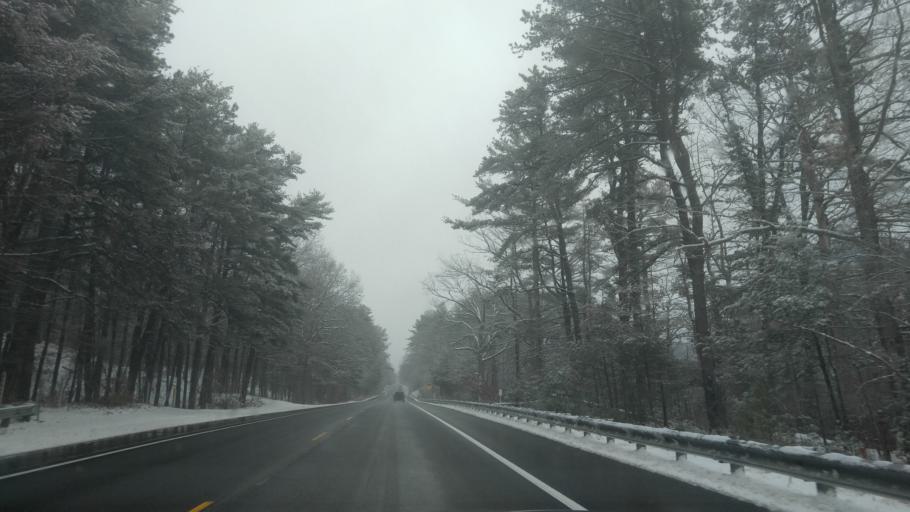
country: US
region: Rhode Island
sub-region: Providence County
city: North Scituate
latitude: 41.8388
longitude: -71.5920
